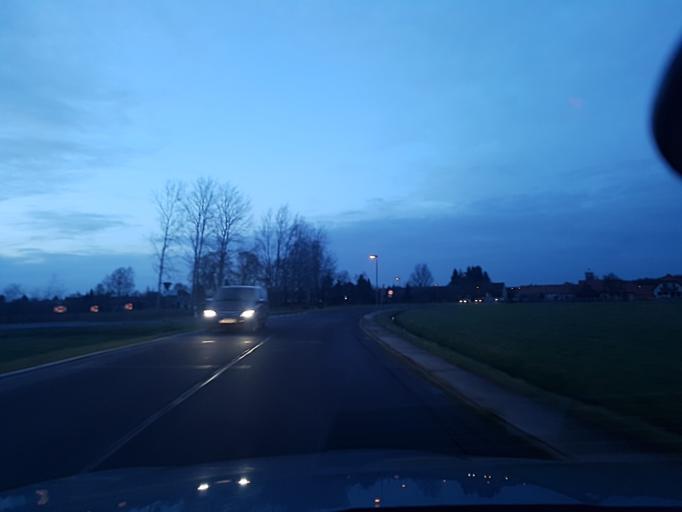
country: DE
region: Brandenburg
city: Ruckersdorf
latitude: 51.5730
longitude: 13.5645
